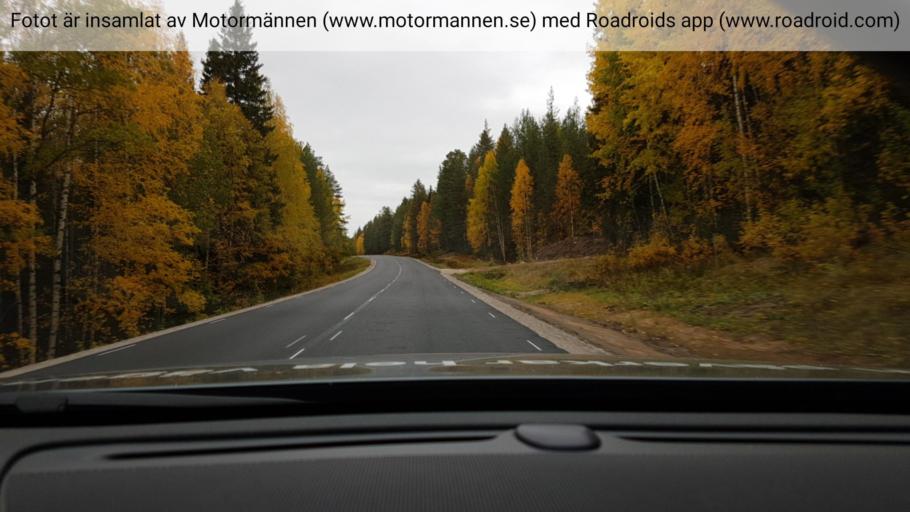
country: SE
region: Norrbotten
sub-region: Overkalix Kommun
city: OEverkalix
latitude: 66.4674
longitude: 22.7927
